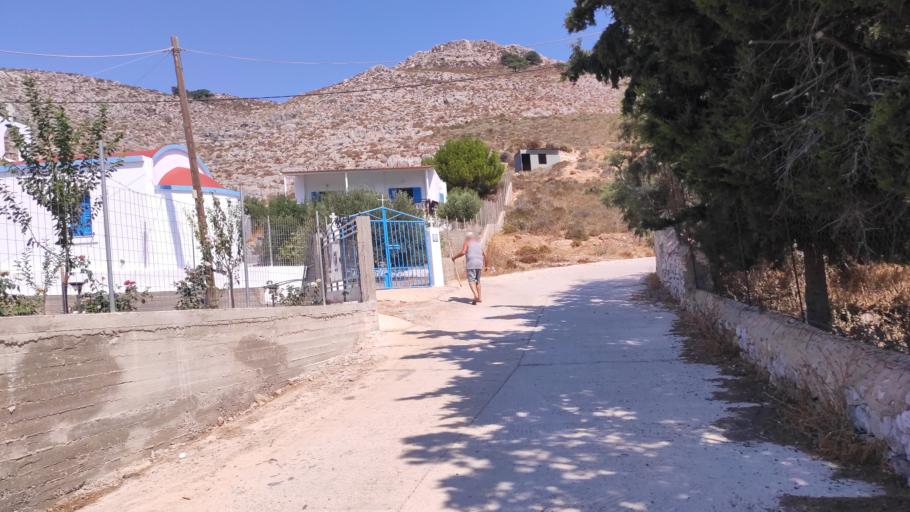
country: GR
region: South Aegean
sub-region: Nomos Dodekanisou
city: Pylion
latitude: 36.9341
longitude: 27.1323
